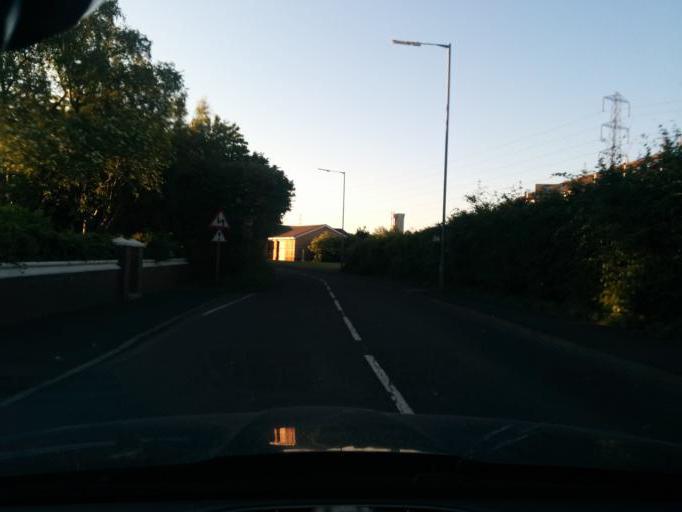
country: GB
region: England
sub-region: Northumberland
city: Cramlington
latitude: 55.1006
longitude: -1.5691
